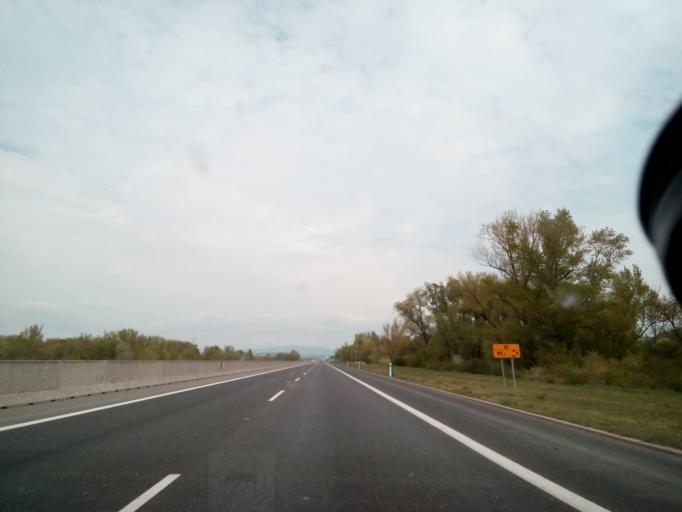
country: SK
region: Trenciansky
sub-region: Okres Nove Mesto nad Vahom
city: Nove Mesto nad Vahom
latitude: 48.6918
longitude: 17.8724
